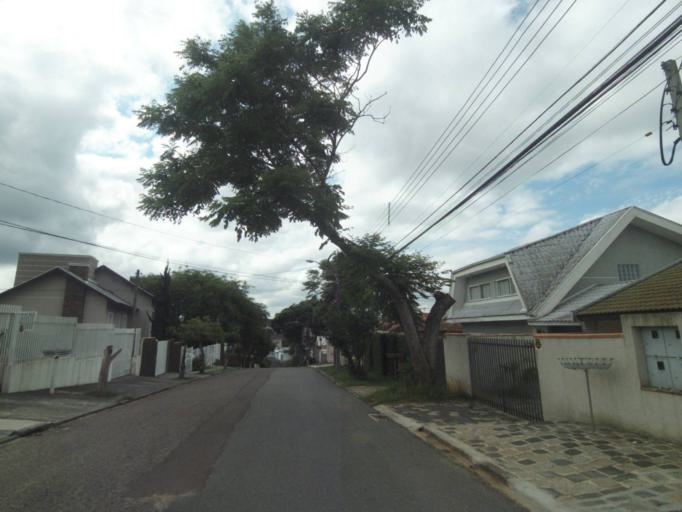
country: BR
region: Parana
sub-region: Curitiba
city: Curitiba
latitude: -25.3816
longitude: -49.2941
